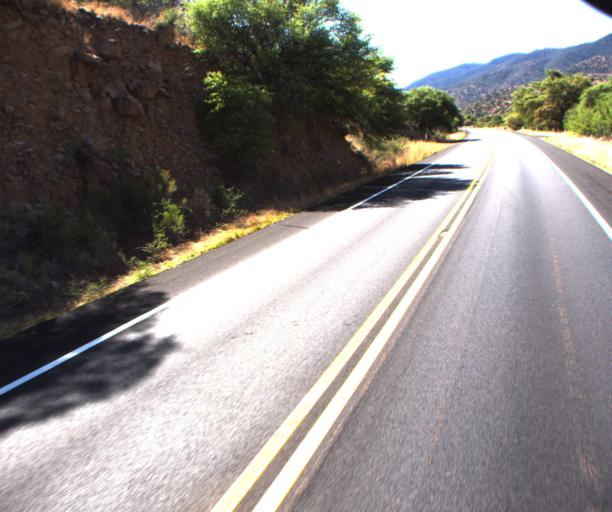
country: US
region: Arizona
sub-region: Cochise County
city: Bisbee
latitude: 31.4910
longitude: -109.9898
